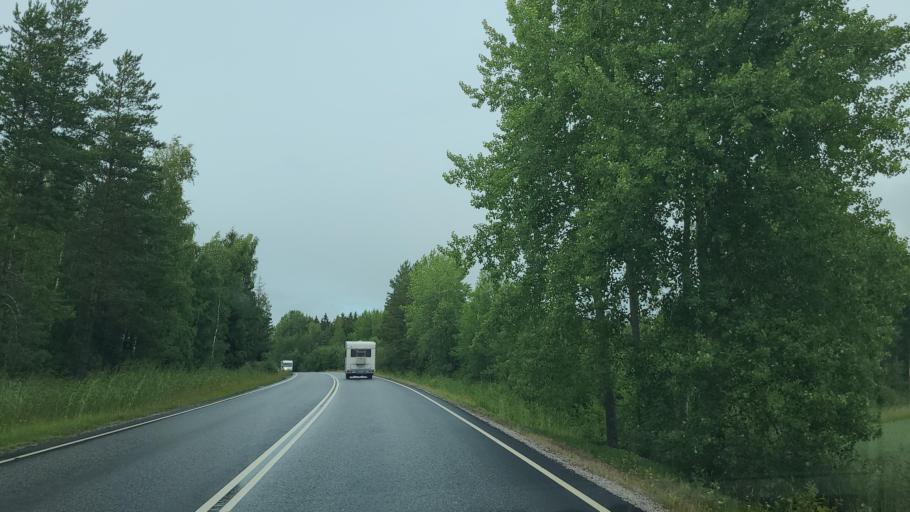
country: FI
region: Varsinais-Suomi
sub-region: Turku
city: Sauvo
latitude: 60.2844
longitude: 22.6733
